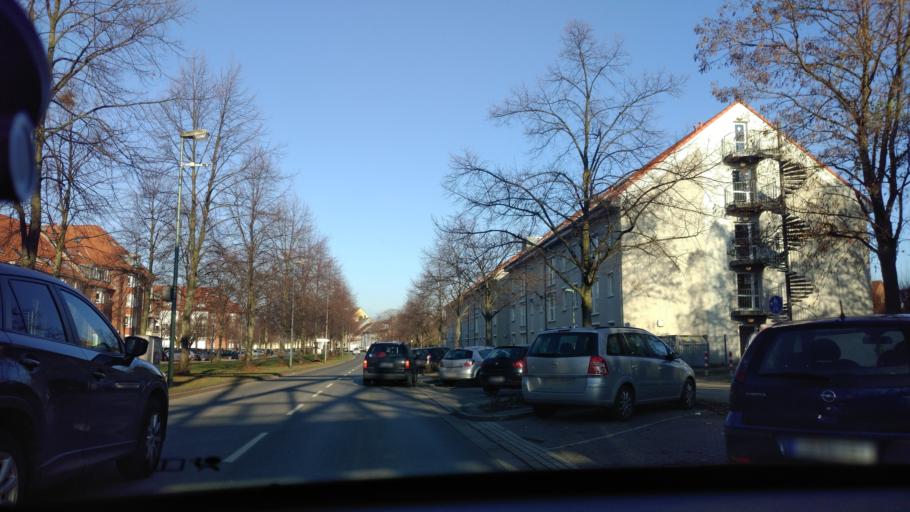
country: DE
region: North Rhine-Westphalia
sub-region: Regierungsbezirk Dusseldorf
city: Essen
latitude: 51.4968
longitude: 7.0102
